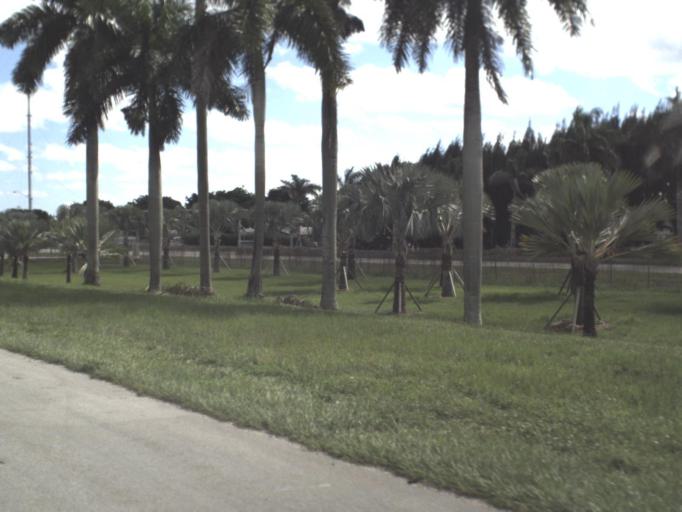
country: US
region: Florida
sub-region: Miami-Dade County
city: Lake Lucerne
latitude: 25.9726
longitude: -80.2356
